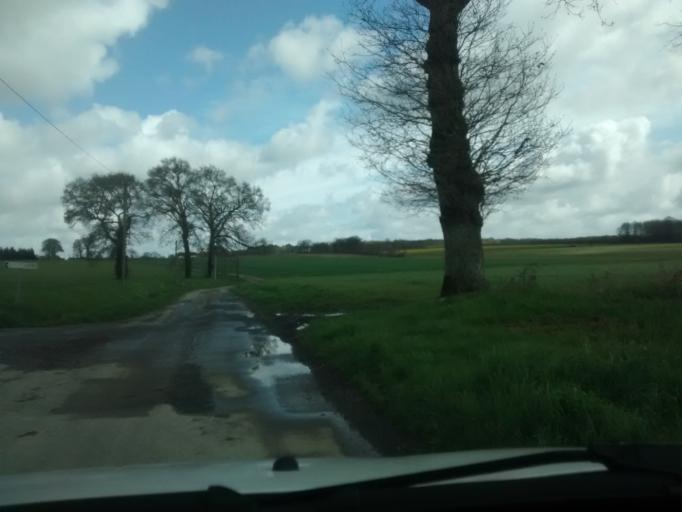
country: FR
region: Brittany
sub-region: Departement d'Ille-et-Vilaine
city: Brece
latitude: 48.1469
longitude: -1.4924
